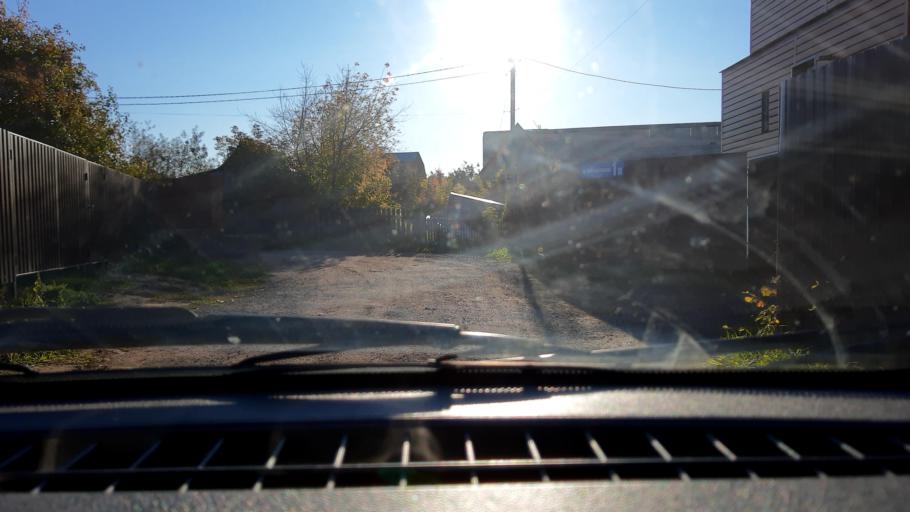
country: RU
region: Bashkortostan
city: Ufa
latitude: 54.6925
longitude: 55.9495
